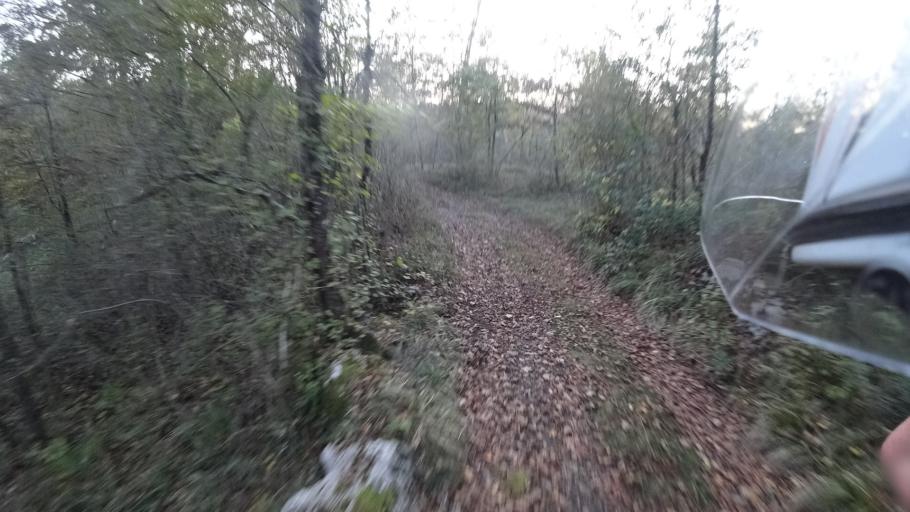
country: HR
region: Primorsko-Goranska
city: Matulji
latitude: 45.4070
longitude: 14.3106
